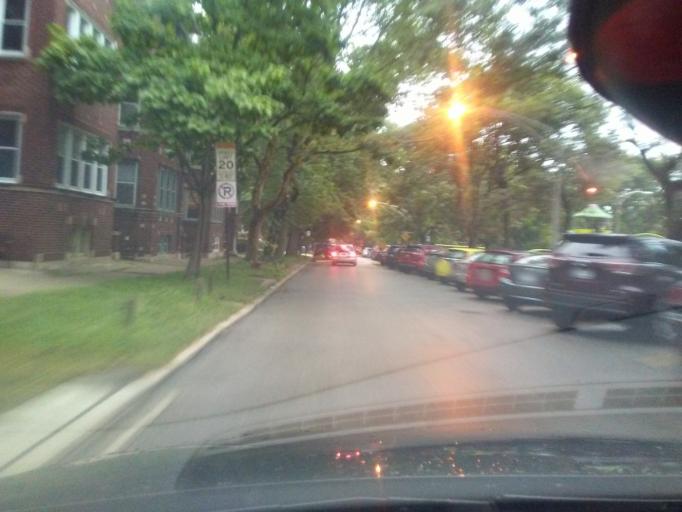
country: US
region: Illinois
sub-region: Cook County
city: Evanston
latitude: 41.9909
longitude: -87.6691
